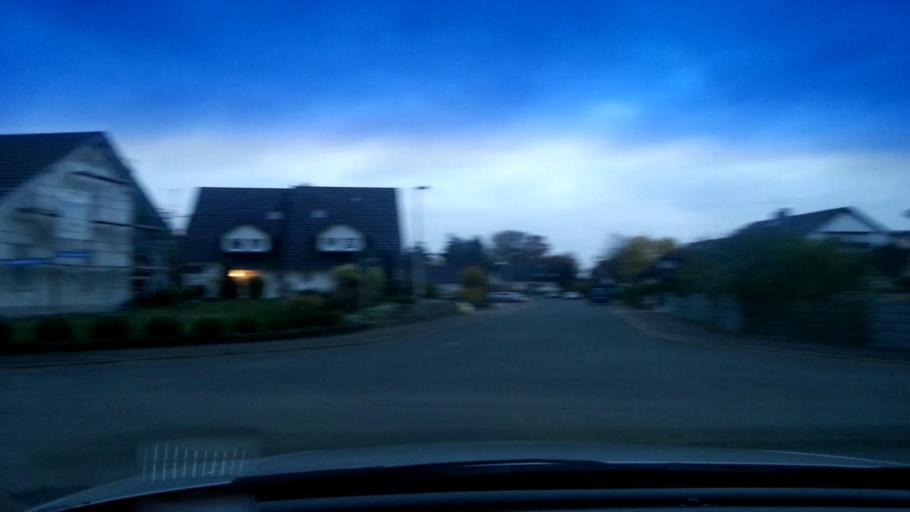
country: DE
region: Bavaria
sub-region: Upper Franconia
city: Kemmern
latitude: 49.9577
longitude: 10.8759
